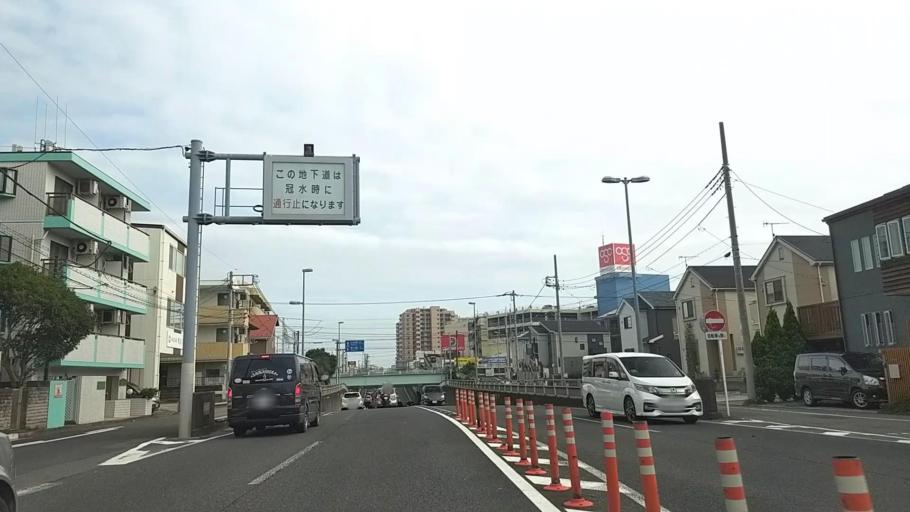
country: JP
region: Kanagawa
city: Hiratsuka
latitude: 35.3309
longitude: 139.3594
